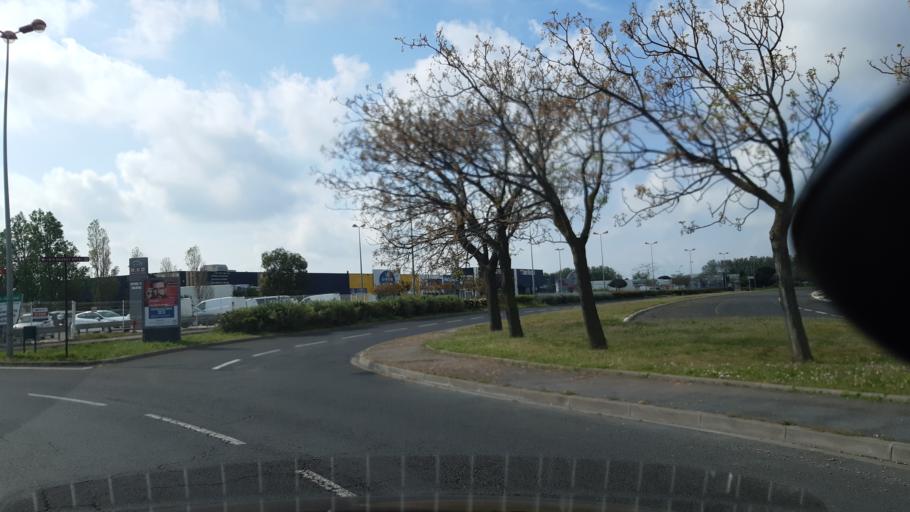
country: FR
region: Languedoc-Roussillon
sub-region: Departement de l'Aude
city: Narbonne
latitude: 43.1792
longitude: 3.0295
